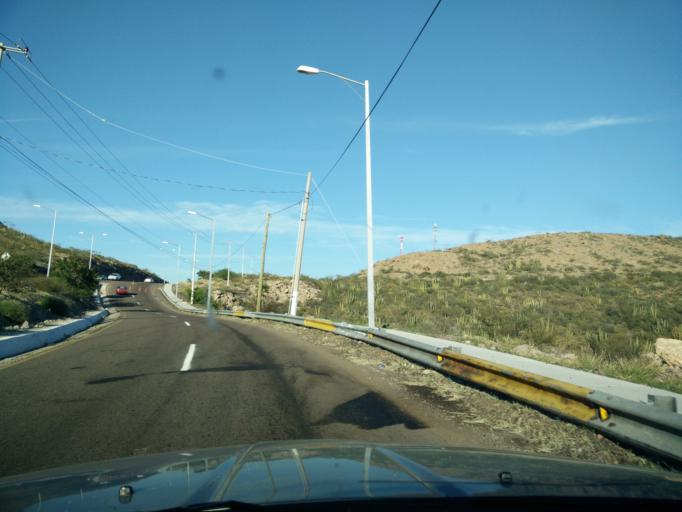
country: MX
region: Sonora
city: Heroica Guaymas
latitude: 27.9517
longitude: -111.0602
